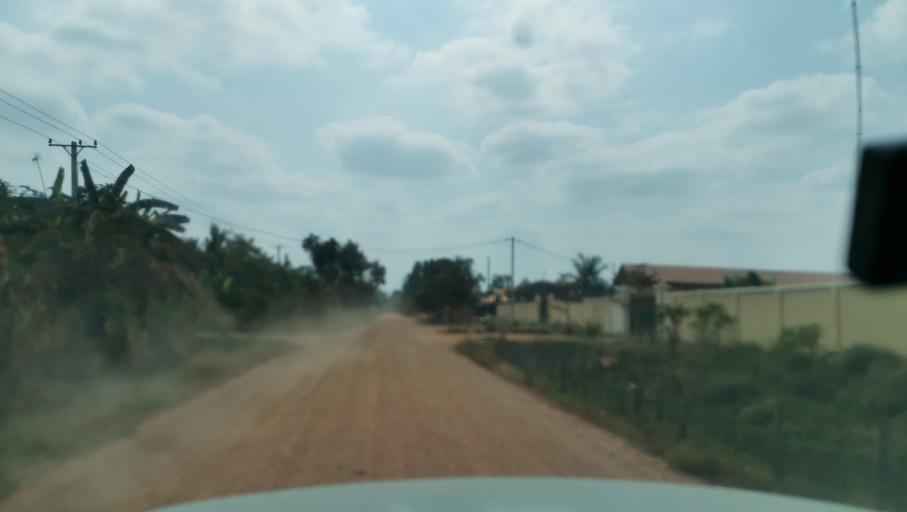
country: KH
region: Battambang
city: Battambang
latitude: 13.0631
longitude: 103.1683
